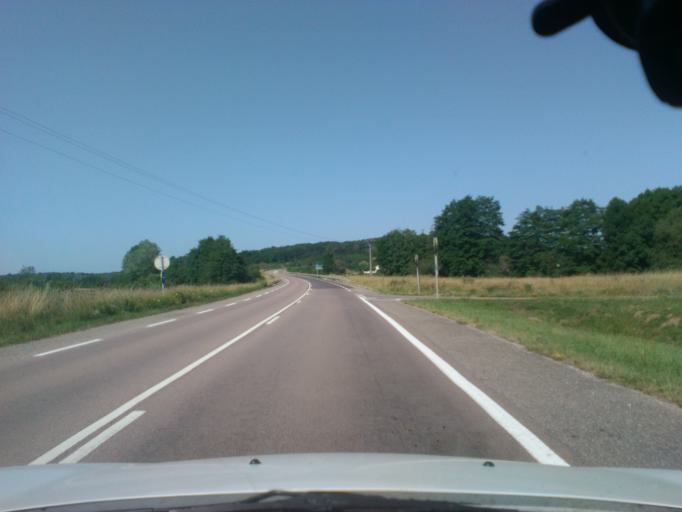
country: FR
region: Lorraine
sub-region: Departement des Vosges
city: Mirecourt
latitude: 48.3078
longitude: 6.0417
